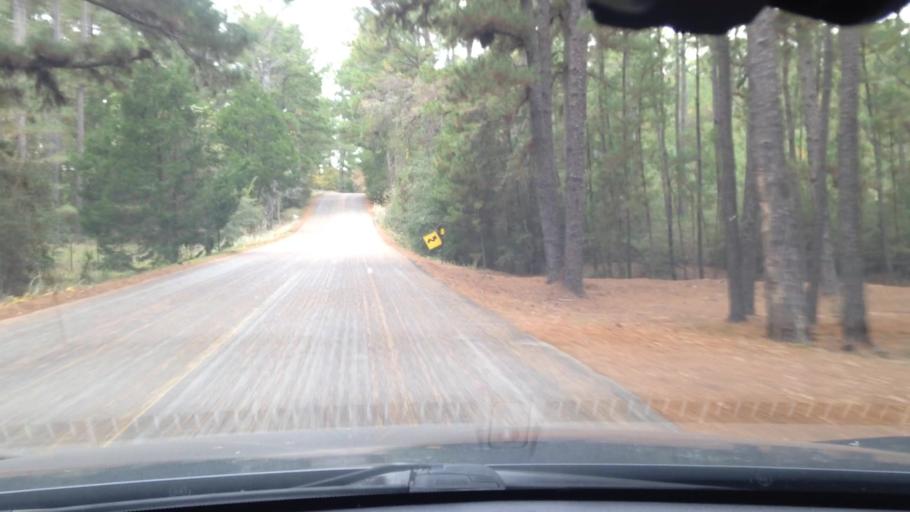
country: US
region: Texas
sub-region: Bastrop County
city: Bastrop
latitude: 30.1267
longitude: -97.2815
